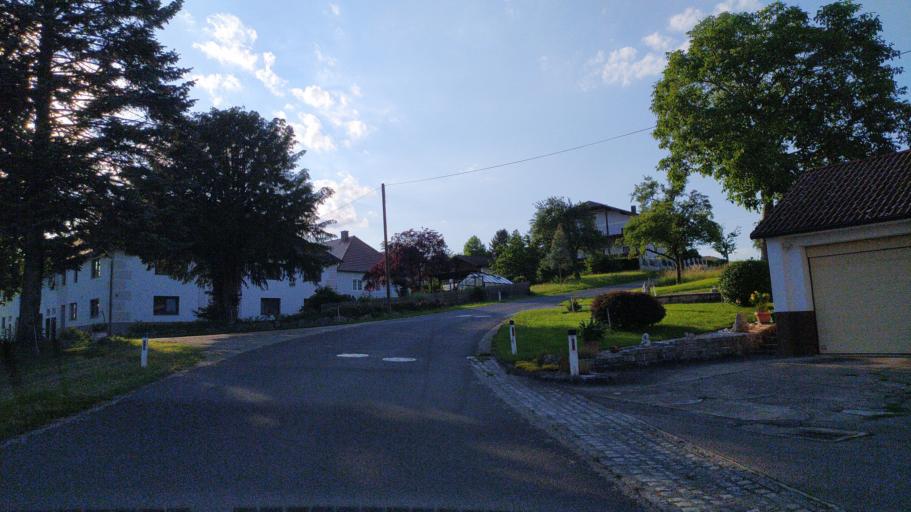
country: AT
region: Lower Austria
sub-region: Politischer Bezirk Amstetten
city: Strengberg
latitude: 48.1510
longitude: 14.6683
